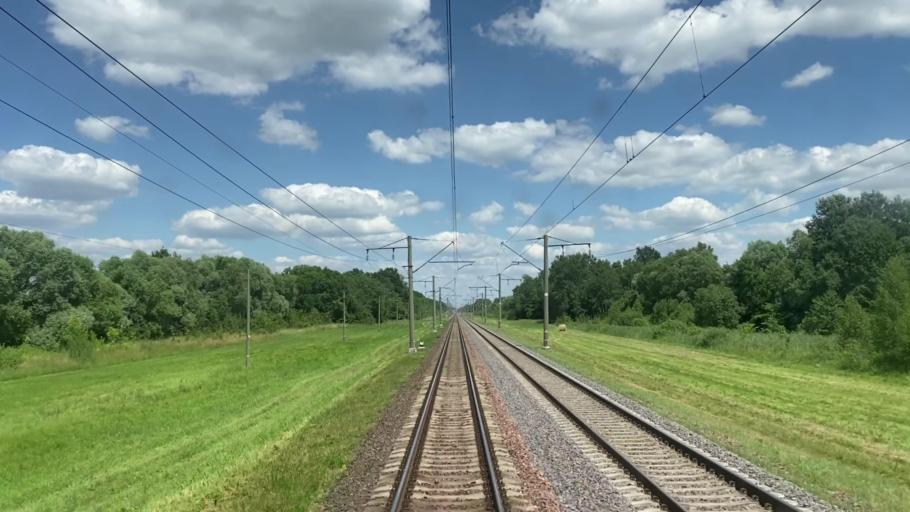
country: BY
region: Brest
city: Zhabinka
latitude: 52.2234
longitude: 24.0671
